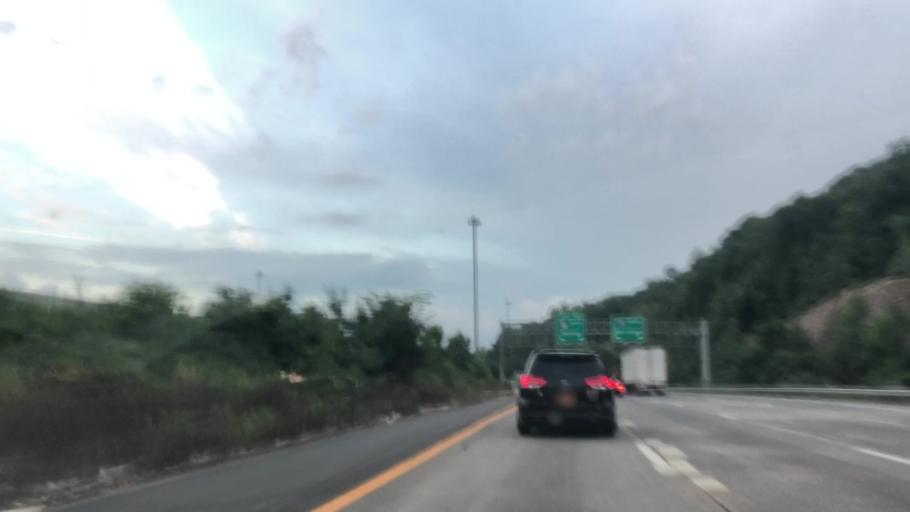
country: US
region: New York
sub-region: Rockland County
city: Suffern
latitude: 41.1073
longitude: -74.1663
